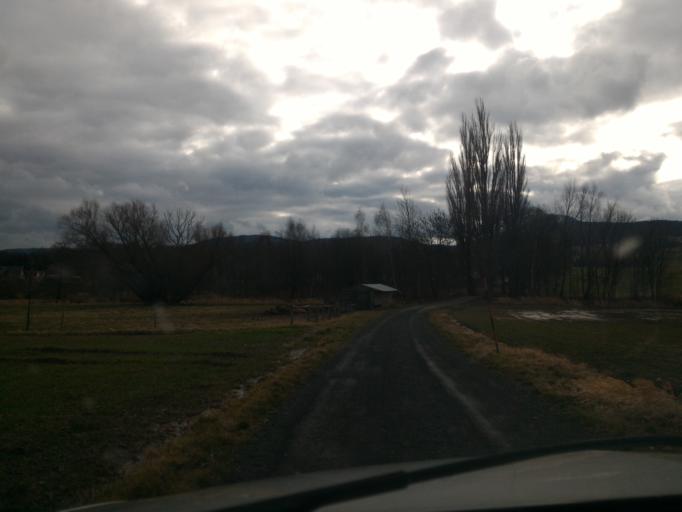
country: CZ
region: Ustecky
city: Varnsdorf
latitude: 50.8871
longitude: 14.6439
